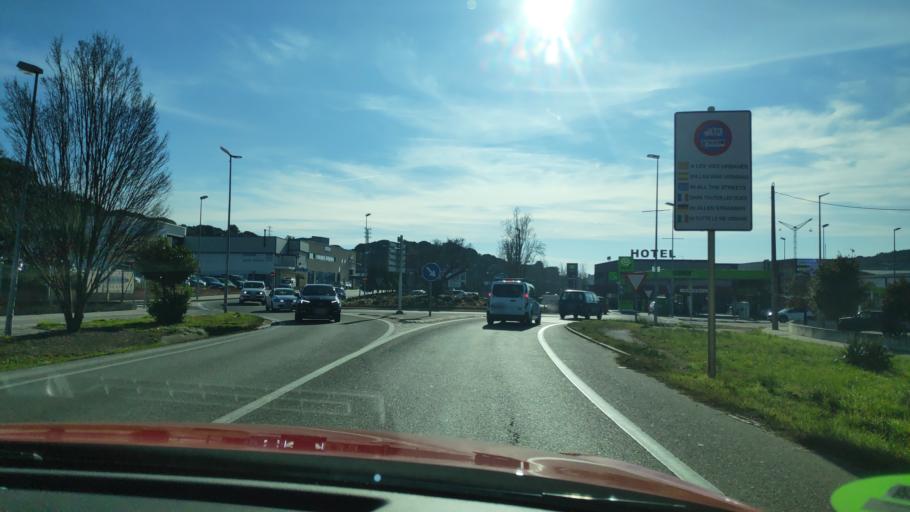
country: ES
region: Catalonia
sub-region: Provincia de Girona
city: Lloret de Mar
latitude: 41.7145
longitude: 2.8307
